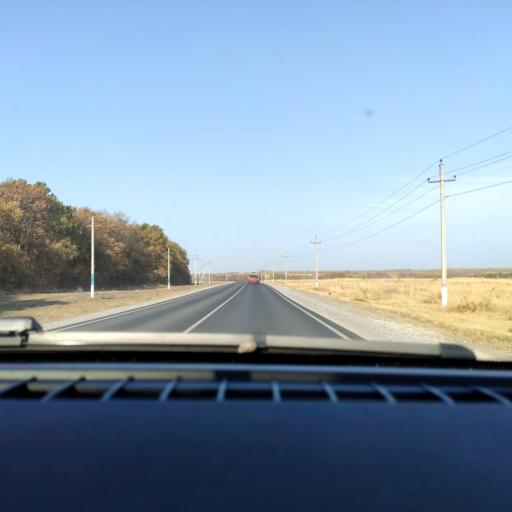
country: RU
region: Voronezj
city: Novaya Usman'
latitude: 51.6889
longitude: 39.3960
